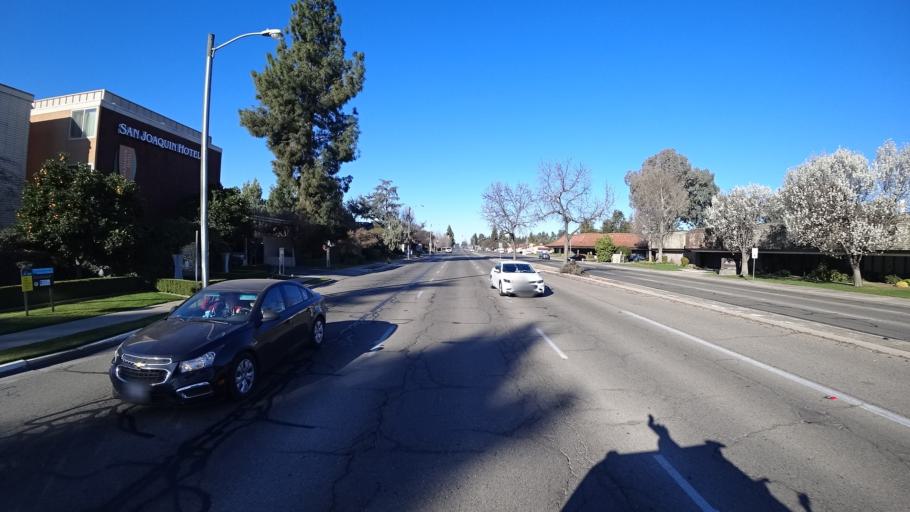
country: US
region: California
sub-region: Fresno County
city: Fresno
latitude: 36.8083
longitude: -119.8156
